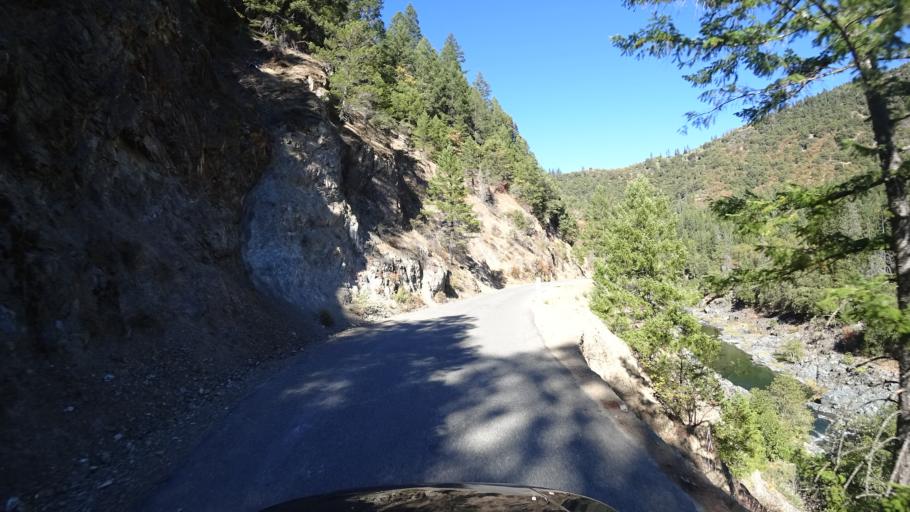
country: US
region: California
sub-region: Humboldt County
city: Willow Creek
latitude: 41.2513
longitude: -123.3066
